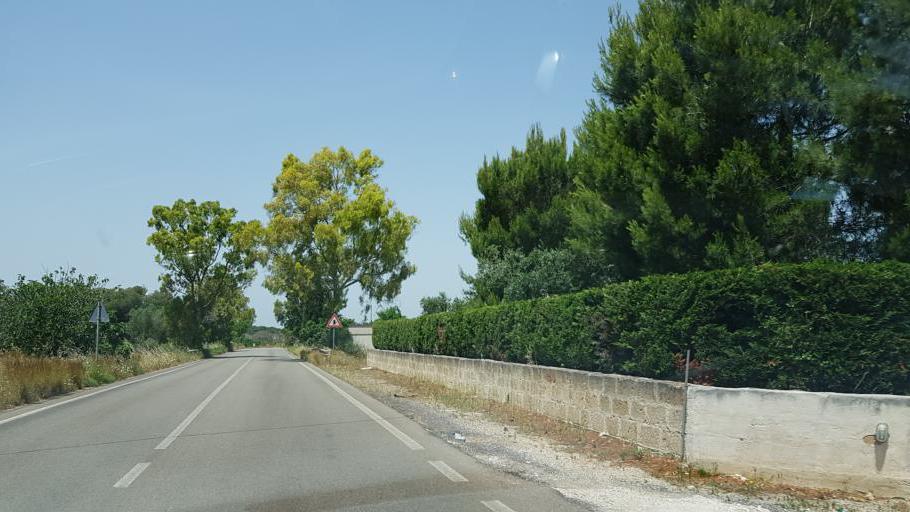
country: IT
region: Apulia
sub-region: Provincia di Lecce
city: Porto Cesareo
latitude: 40.2633
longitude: 17.9178
